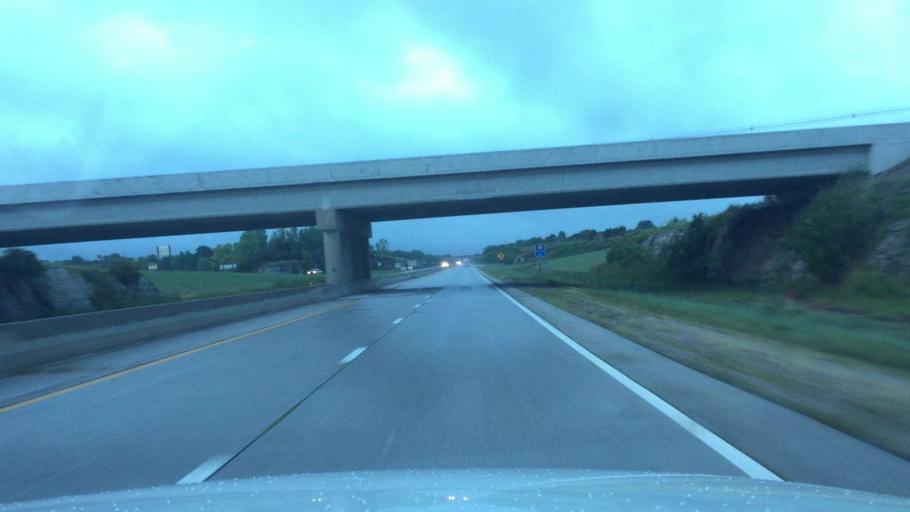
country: US
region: Kansas
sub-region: Neosho County
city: Chanute
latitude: 37.6896
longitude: -95.4796
